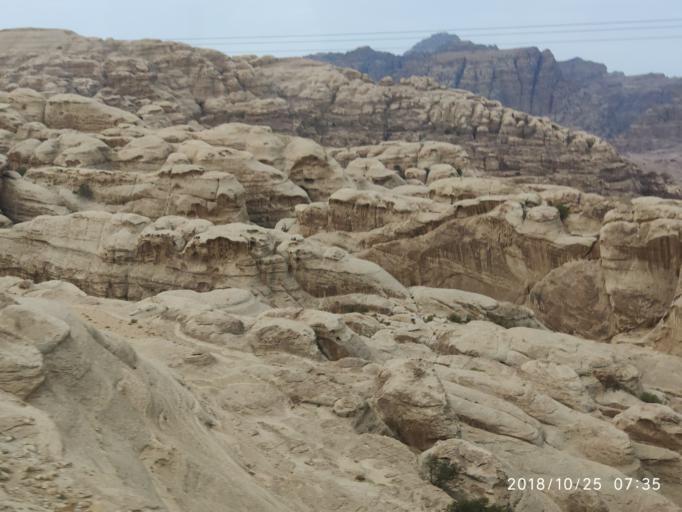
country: JO
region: Ma'an
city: Petra
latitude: 30.3360
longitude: 35.4679
